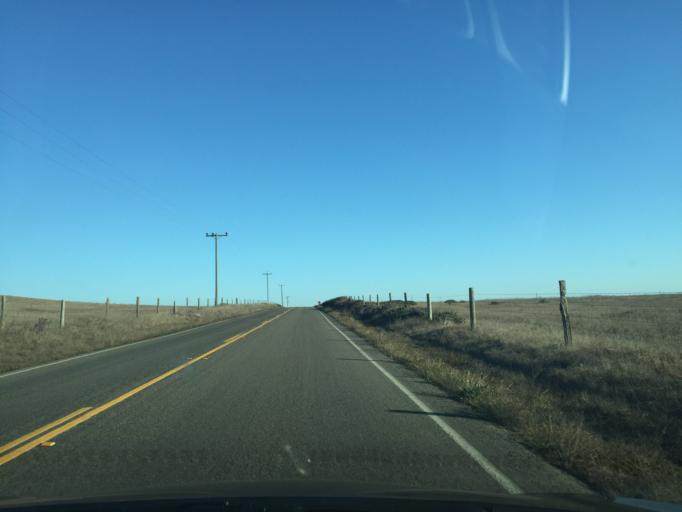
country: US
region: California
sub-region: San Luis Obispo County
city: Cambria
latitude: 35.6729
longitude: -121.2813
